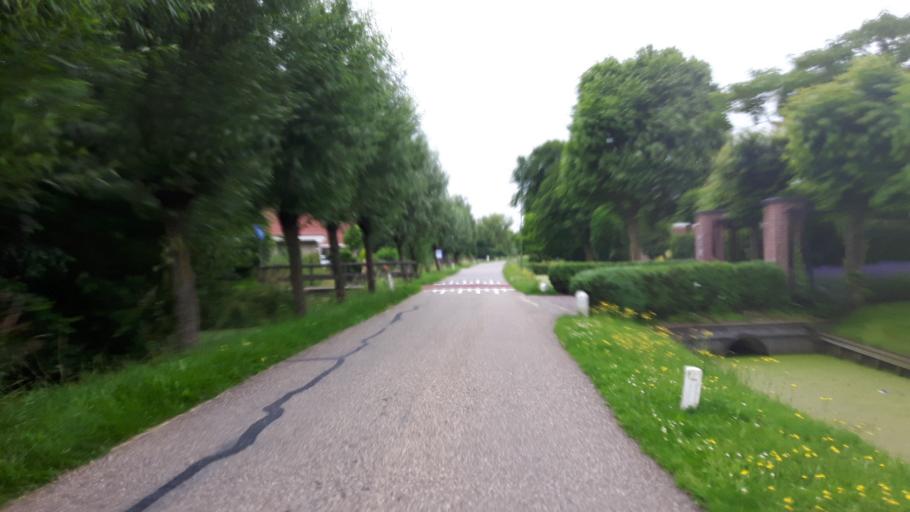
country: NL
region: South Holland
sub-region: Gemeente Schoonhoven
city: Schoonhoven
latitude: 51.9430
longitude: 4.8675
